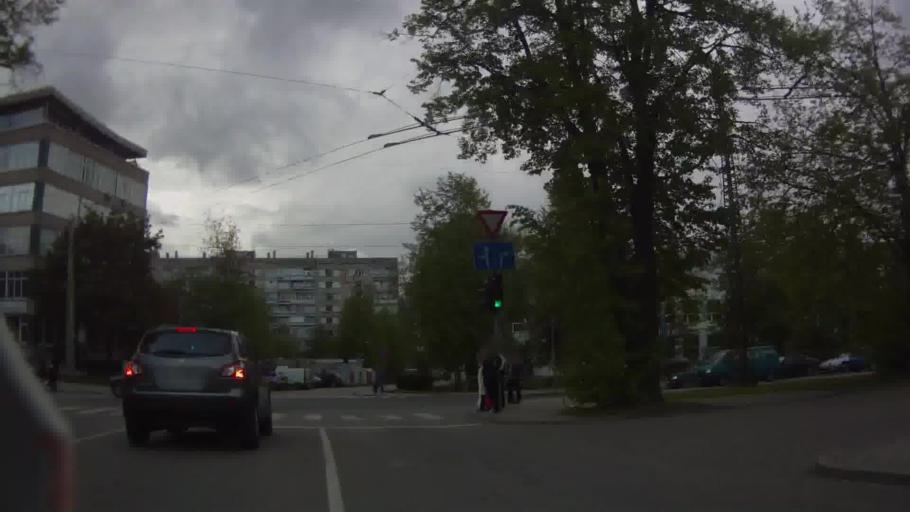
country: LV
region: Riga
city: Riga
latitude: 56.9737
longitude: 24.1358
